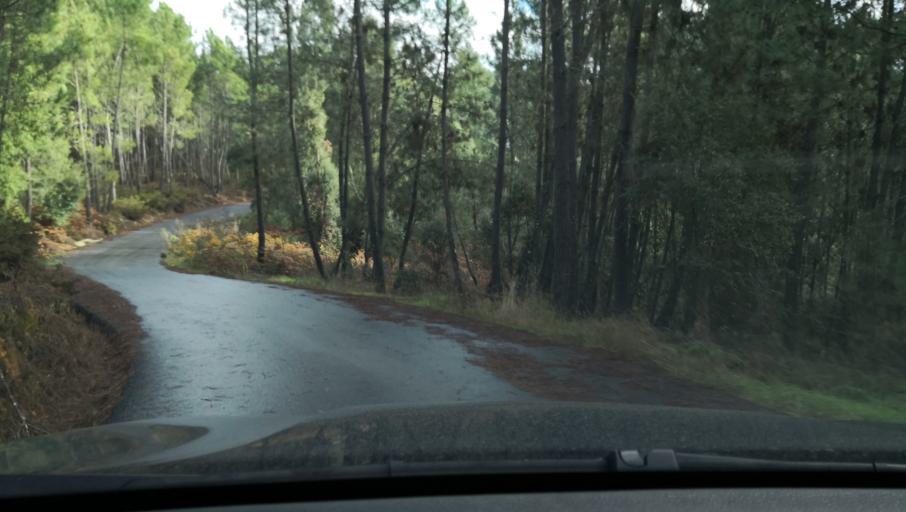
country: PT
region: Vila Real
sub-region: Vila Real
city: Vila Real
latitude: 41.2667
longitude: -7.7196
